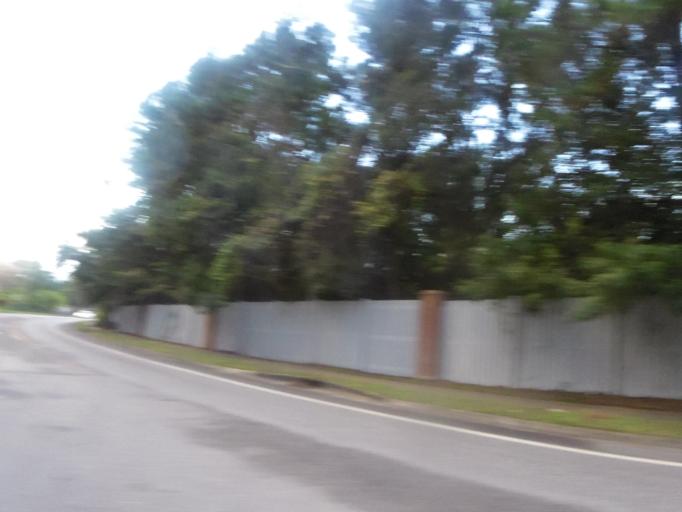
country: US
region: Florida
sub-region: Duval County
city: Jacksonville
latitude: 30.2318
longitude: -81.5989
